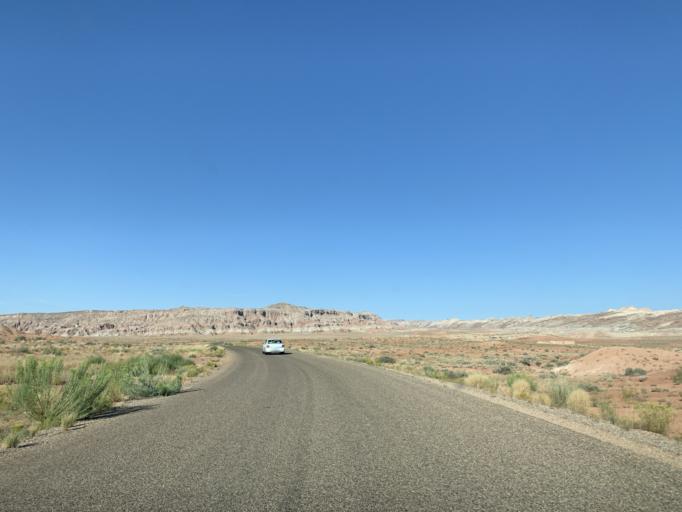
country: US
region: Utah
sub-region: Emery County
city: Ferron
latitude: 38.5808
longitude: -110.7273
